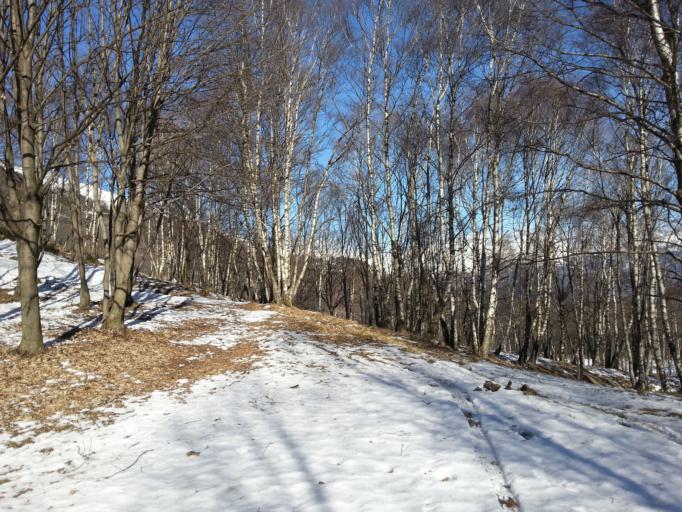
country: IT
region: Lombardy
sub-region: Provincia di Como
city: San Siro
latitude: 46.0694
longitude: 9.2487
